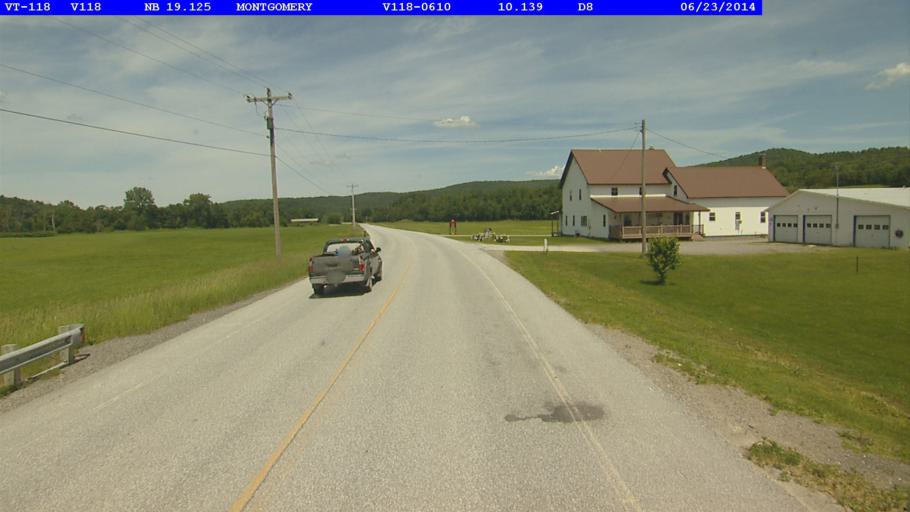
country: US
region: Vermont
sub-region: Franklin County
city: Richford
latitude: 44.9161
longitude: -72.6692
